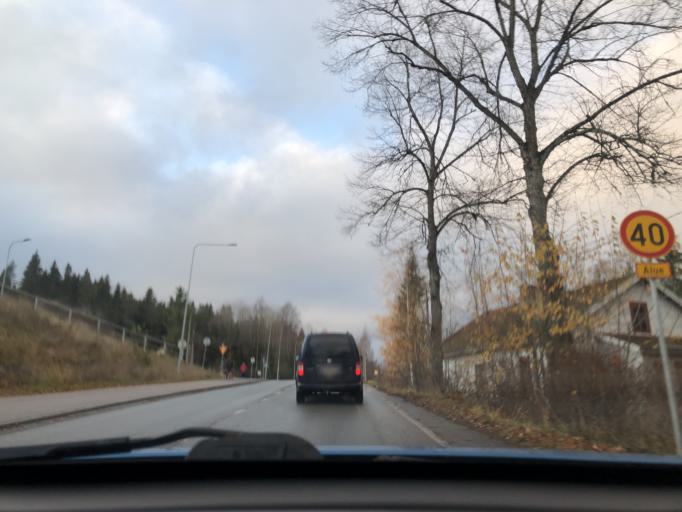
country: FI
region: Pirkanmaa
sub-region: Tampere
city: Kangasala
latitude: 61.4671
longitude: 24.0652
